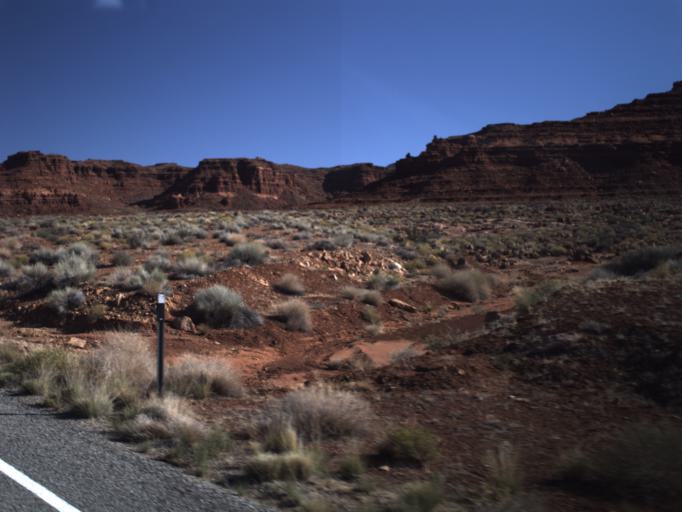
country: US
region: Utah
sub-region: San Juan County
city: Blanding
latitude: 37.8403
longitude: -110.3560
